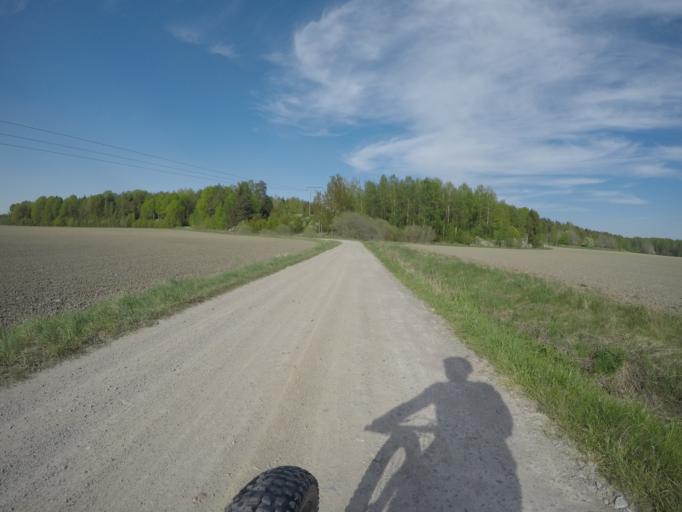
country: SE
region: Vaestmanland
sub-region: Vasteras
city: Vasteras
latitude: 59.6568
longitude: 16.4982
